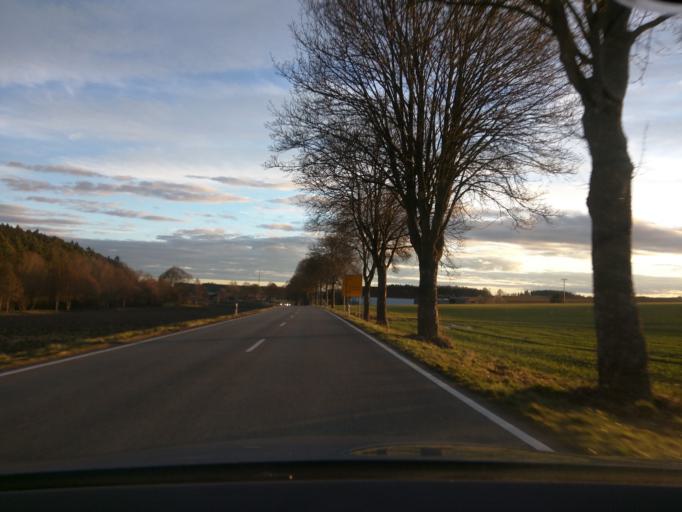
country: DE
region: Bavaria
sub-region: Upper Bavaria
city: Attenkirchen
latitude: 48.4832
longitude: 11.7593
